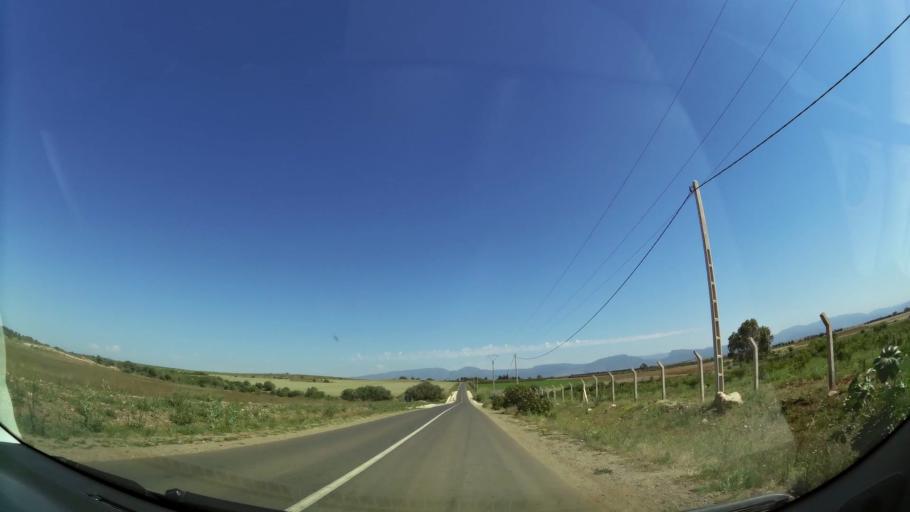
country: MA
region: Oriental
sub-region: Berkane-Taourirt
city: Madagh
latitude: 35.0347
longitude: -2.4179
